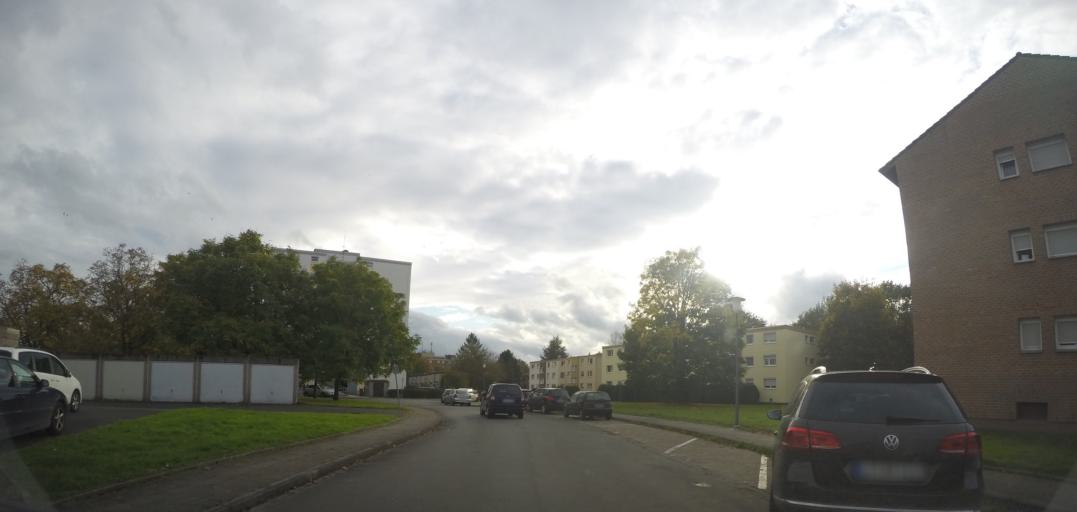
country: DE
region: North Rhine-Westphalia
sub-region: Regierungsbezirk Arnsberg
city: Lippstadt
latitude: 51.6646
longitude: 8.3251
